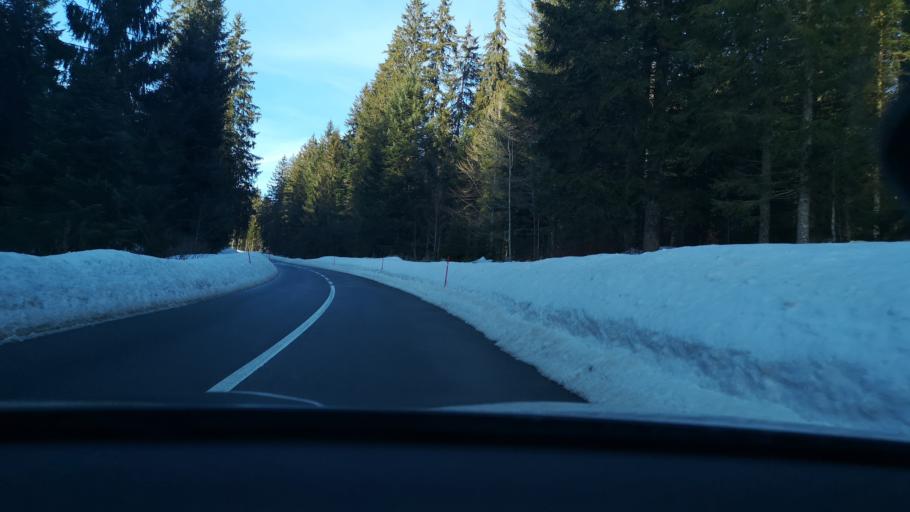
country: CH
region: Neuchatel
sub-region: Val-de-Travers District
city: Fleurier
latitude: 46.9303
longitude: 6.5316
